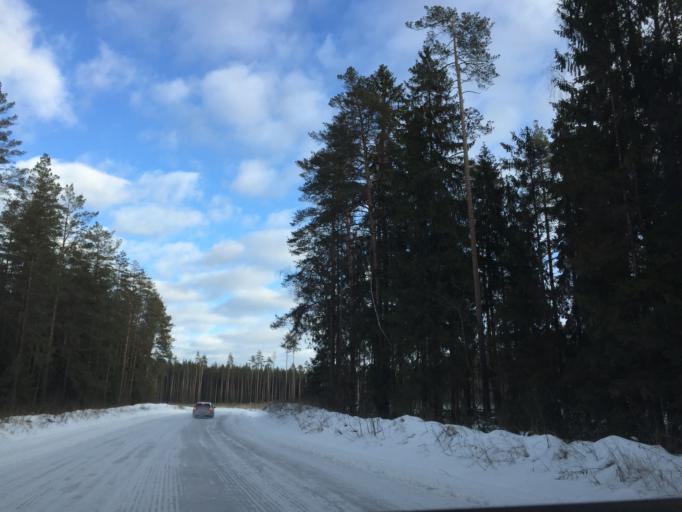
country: LV
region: Ogre
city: Jumprava
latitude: 56.5775
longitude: 24.9460
